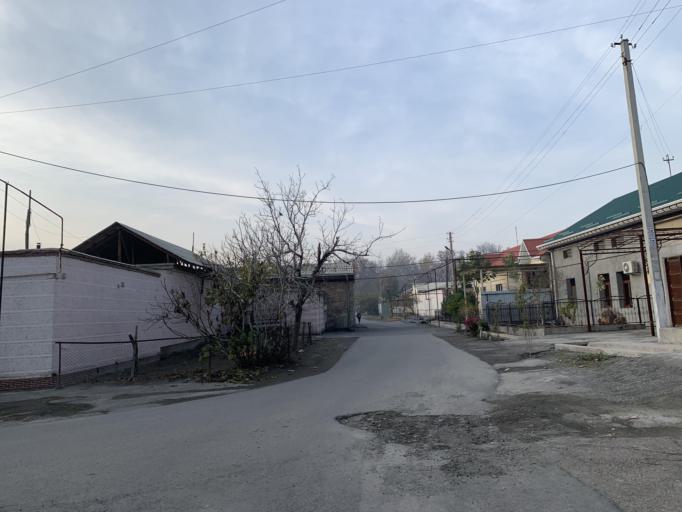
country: UZ
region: Fergana
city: Qo`qon
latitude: 40.5423
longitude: 70.9270
